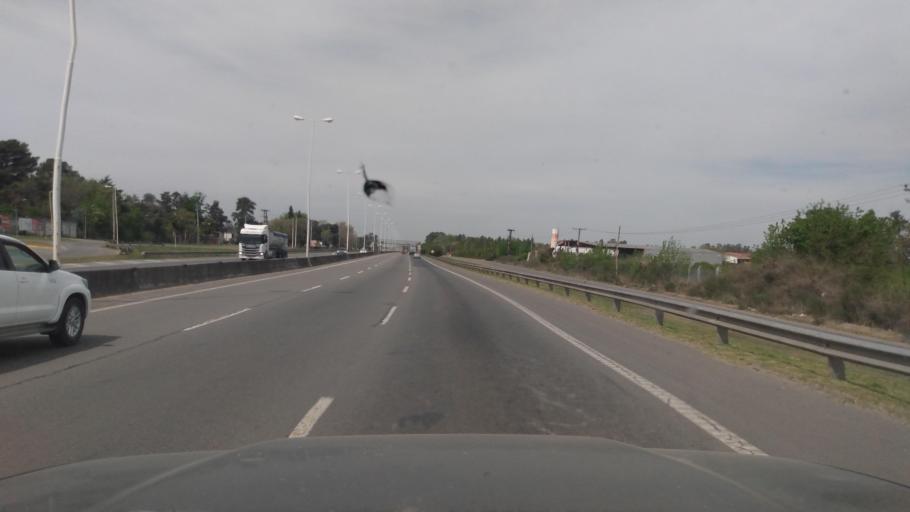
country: AR
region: Buenos Aires
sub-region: Partido de Pilar
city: Pilar
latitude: -34.4190
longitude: -59.0027
